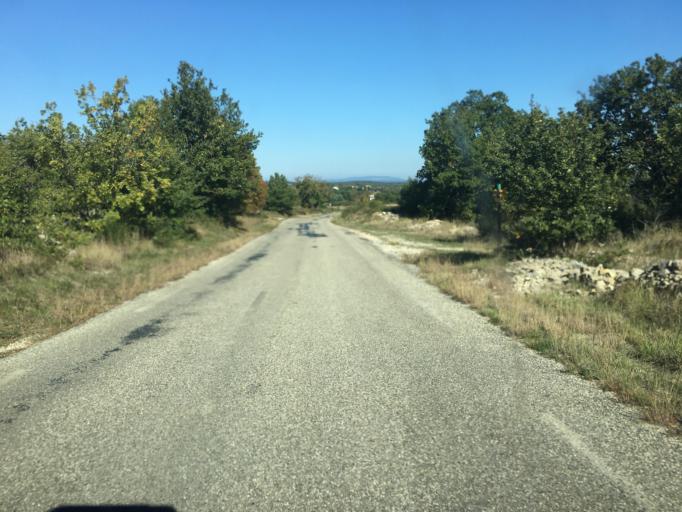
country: FR
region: Languedoc-Roussillon
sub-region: Departement du Gard
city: Barjac
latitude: 44.1766
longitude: 4.3244
